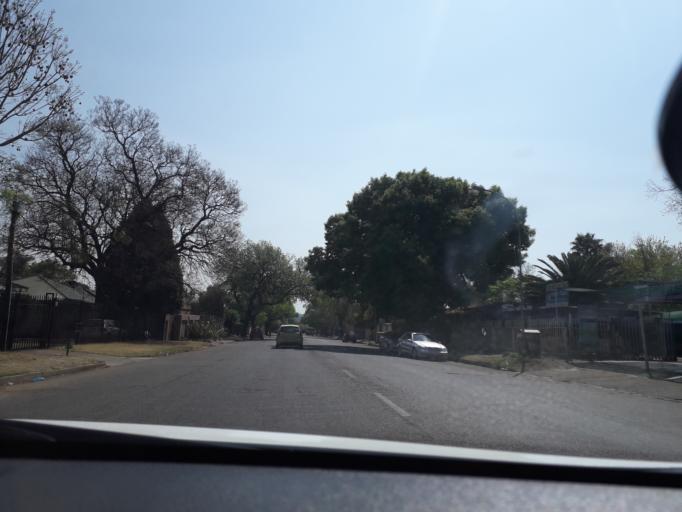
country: ZA
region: Gauteng
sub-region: City of Johannesburg Metropolitan Municipality
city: Modderfontein
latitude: -26.0973
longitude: 28.2306
